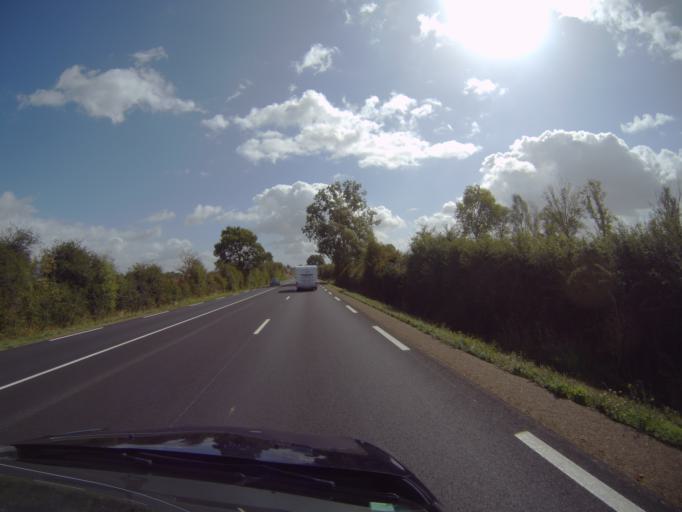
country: FR
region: Pays de la Loire
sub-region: Departement de Maine-et-Loire
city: Nueil-sur-Layon
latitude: 47.1686
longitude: -0.3681
